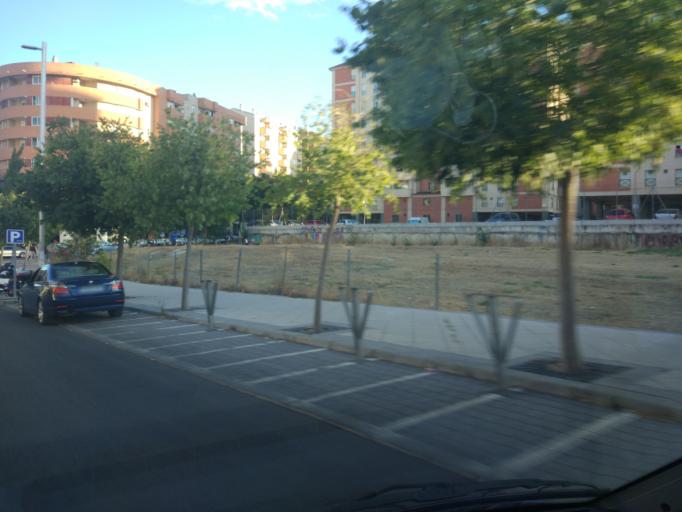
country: ES
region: Andalusia
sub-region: Provincia de Jaen
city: Jaen
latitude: 37.7868
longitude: -3.7779
